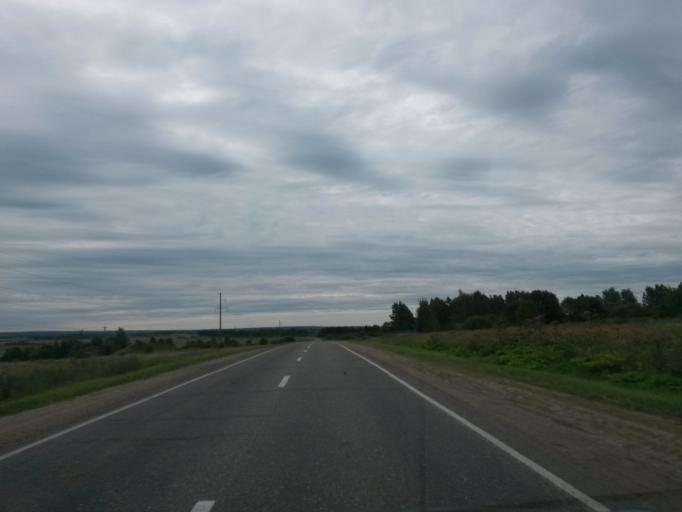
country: RU
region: Jaroslavl
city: Gavrilov-Yam
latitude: 57.3546
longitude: 39.7854
